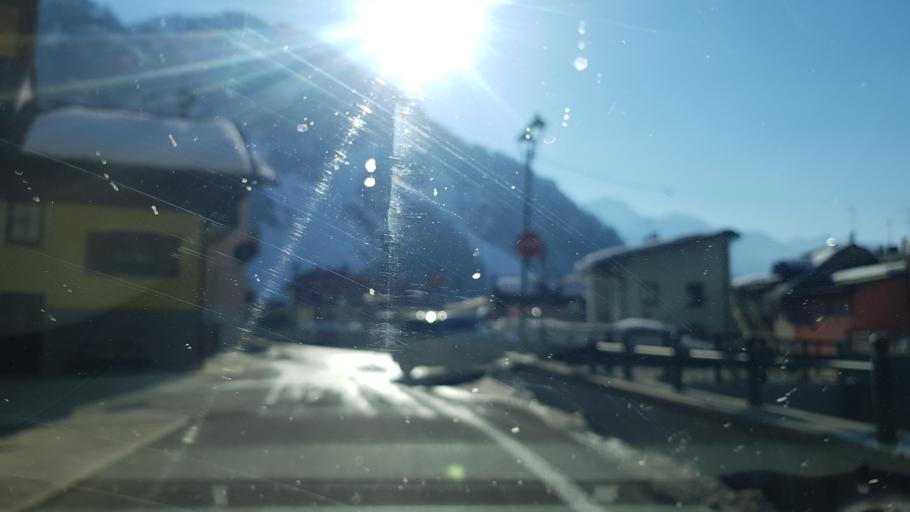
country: IT
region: Friuli Venezia Giulia
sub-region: Provincia di Udine
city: Malborghetto
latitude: 46.5115
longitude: 13.4724
